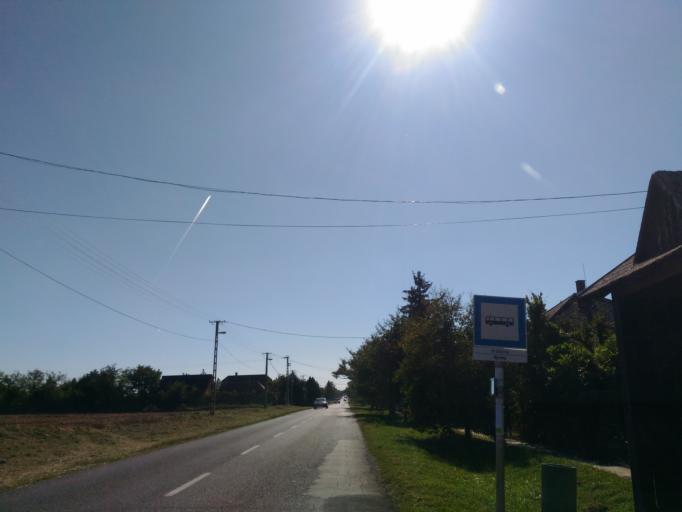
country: HU
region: Fejer
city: Ivancsa
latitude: 47.1693
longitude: 18.8179
